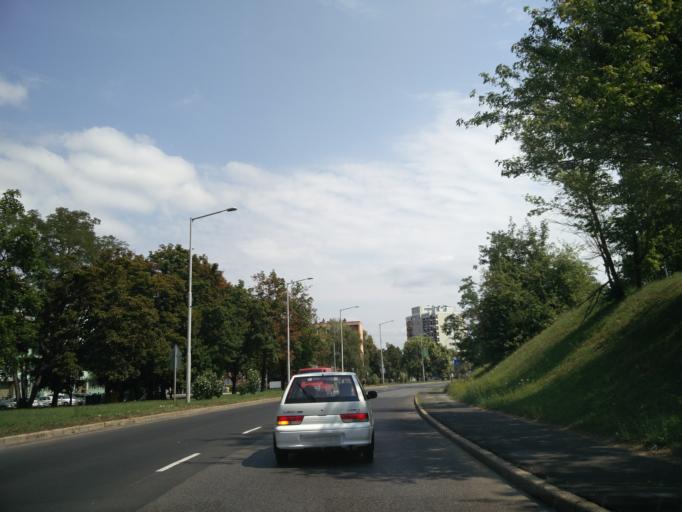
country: HU
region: Zala
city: Zalaegerszeg
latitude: 46.8331
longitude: 16.8283
